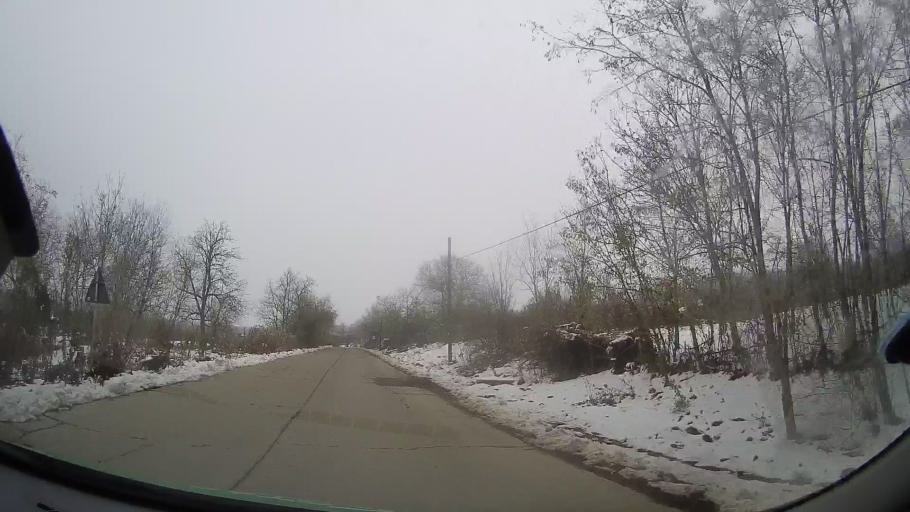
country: RO
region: Vrancea
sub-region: Comuna Boghesti
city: Boghesti
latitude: 46.2051
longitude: 27.4410
